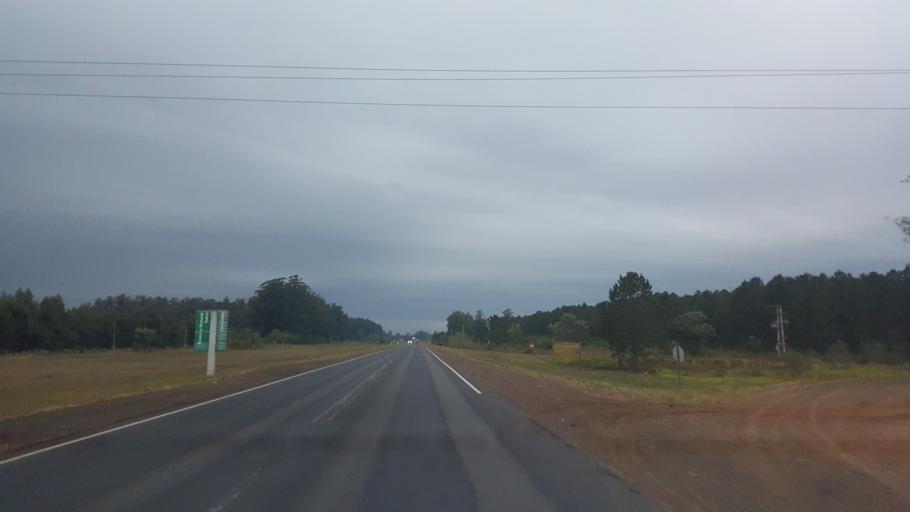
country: AR
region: Corrientes
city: Ituzaingo
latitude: -27.6072
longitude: -56.4424
